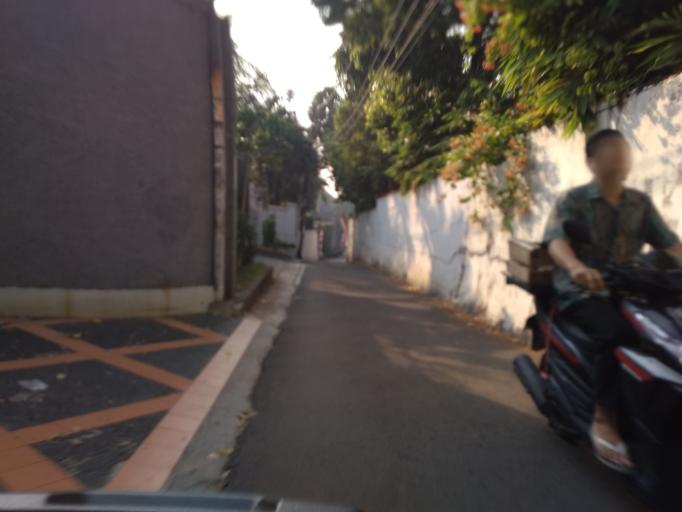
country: ID
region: Jakarta Raya
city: Jakarta
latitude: -6.2762
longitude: 106.8164
